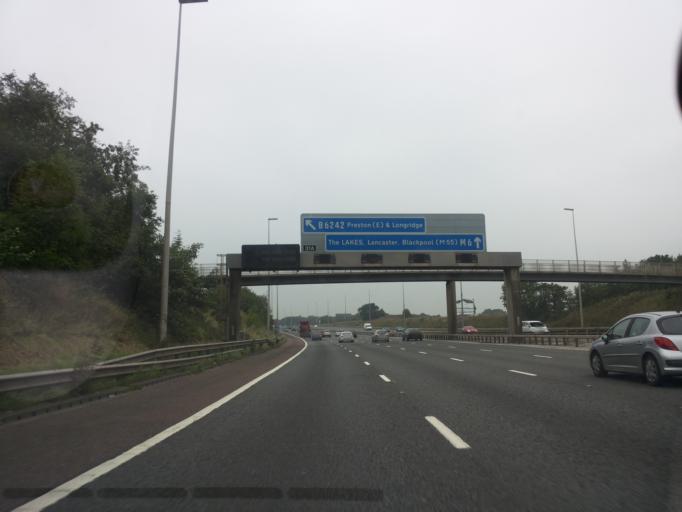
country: GB
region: England
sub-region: Lancashire
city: Goosnargh
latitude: 53.7855
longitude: -2.6528
